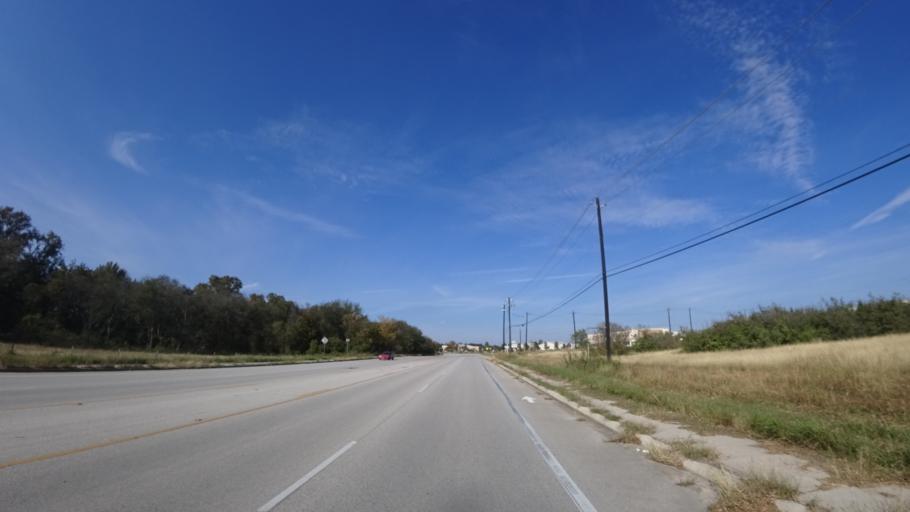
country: US
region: Texas
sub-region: Travis County
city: Pflugerville
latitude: 30.3981
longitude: -97.6332
